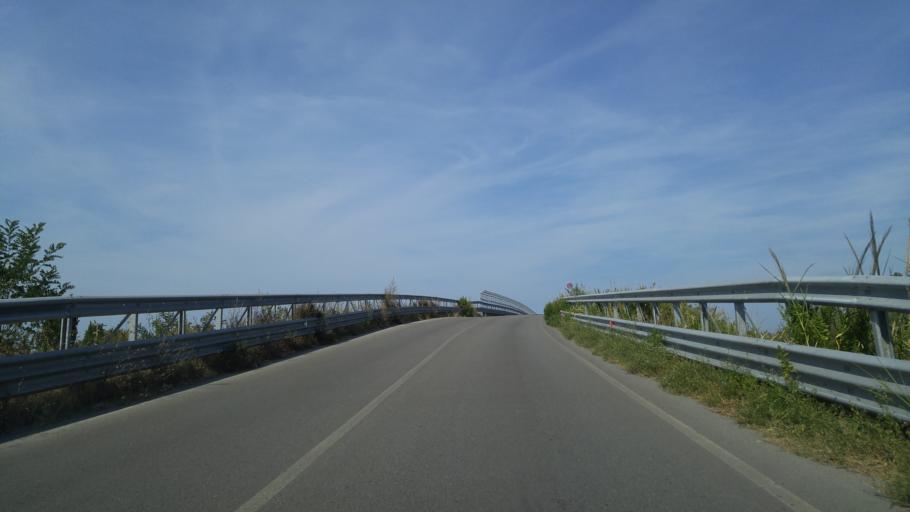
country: IT
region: The Marches
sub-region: Provincia di Pesaro e Urbino
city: Rosciano
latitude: 43.8154
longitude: 13.0078
